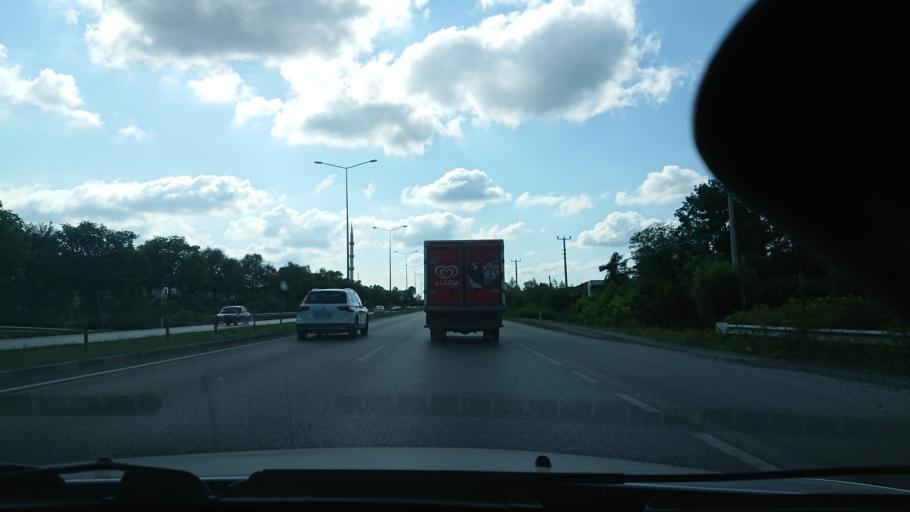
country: TR
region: Samsun
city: Terme
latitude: 41.2156
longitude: 36.9305
